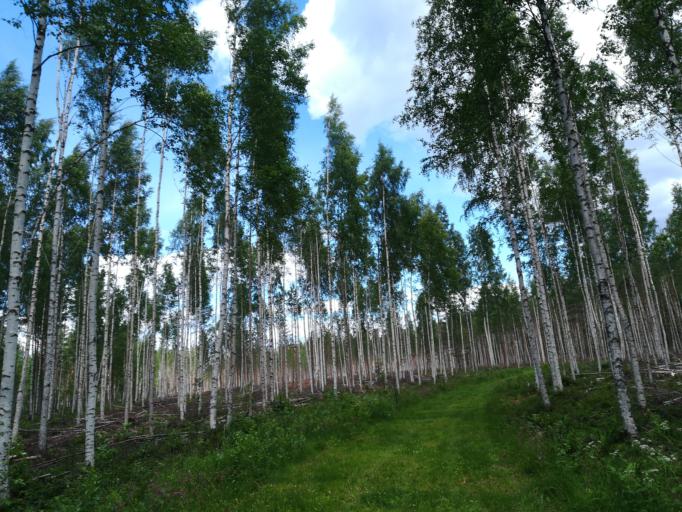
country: FI
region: Southern Savonia
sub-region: Mikkeli
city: Hirvensalmi
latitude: 61.6530
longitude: 26.7808
